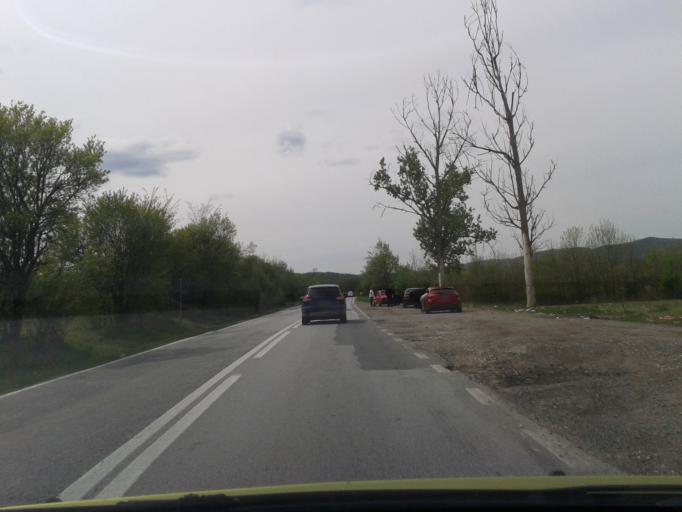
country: RO
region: Hunedoara
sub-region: Comuna Dobra
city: Dobra
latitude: 45.9109
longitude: 22.5453
